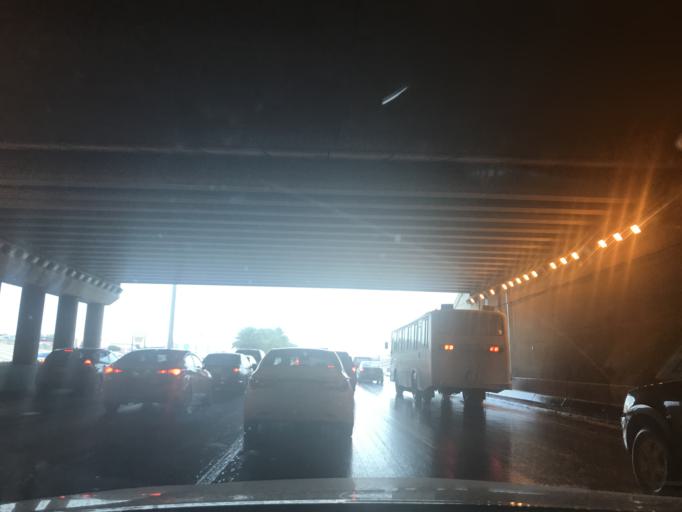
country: SA
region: Ar Riyad
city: Riyadh
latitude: 24.7761
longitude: 46.7305
